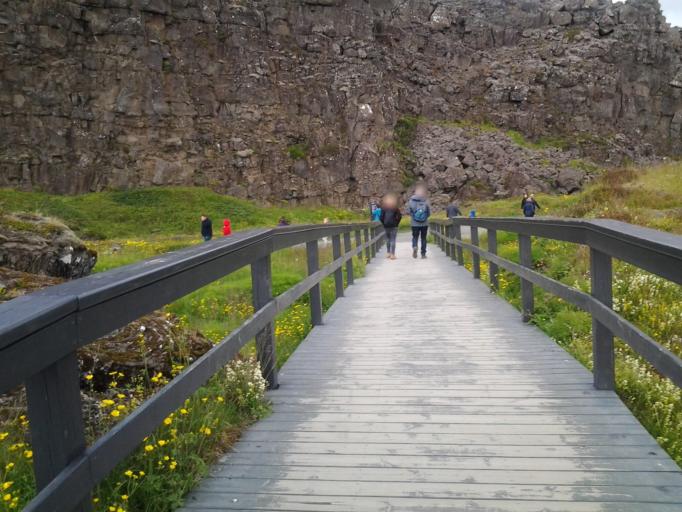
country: IS
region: South
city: Hveragerdi
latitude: 64.2600
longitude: -21.1223
